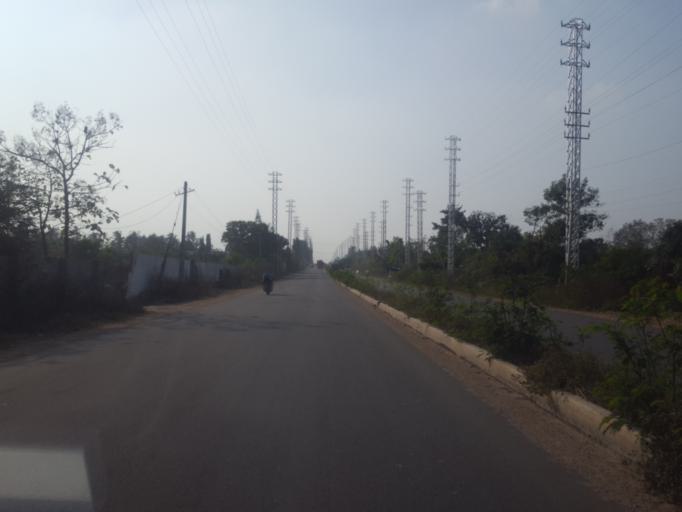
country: IN
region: Telangana
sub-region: Medak
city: Serilingampalle
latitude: 17.4184
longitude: 78.2405
